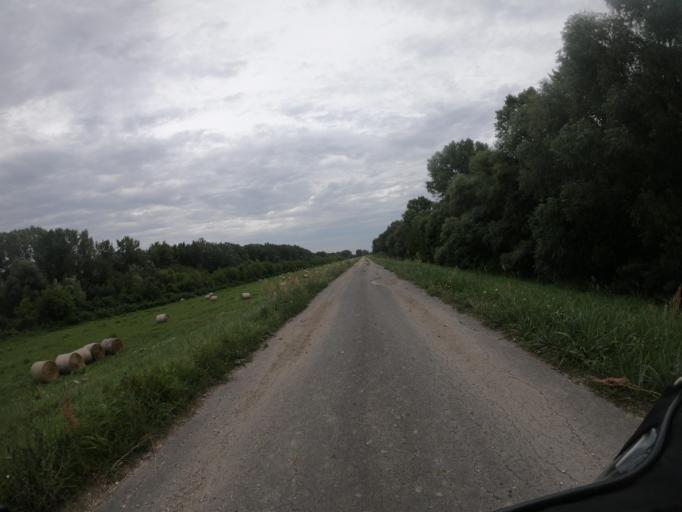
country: HU
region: Hajdu-Bihar
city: Egyek
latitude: 47.6878
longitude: 20.8839
